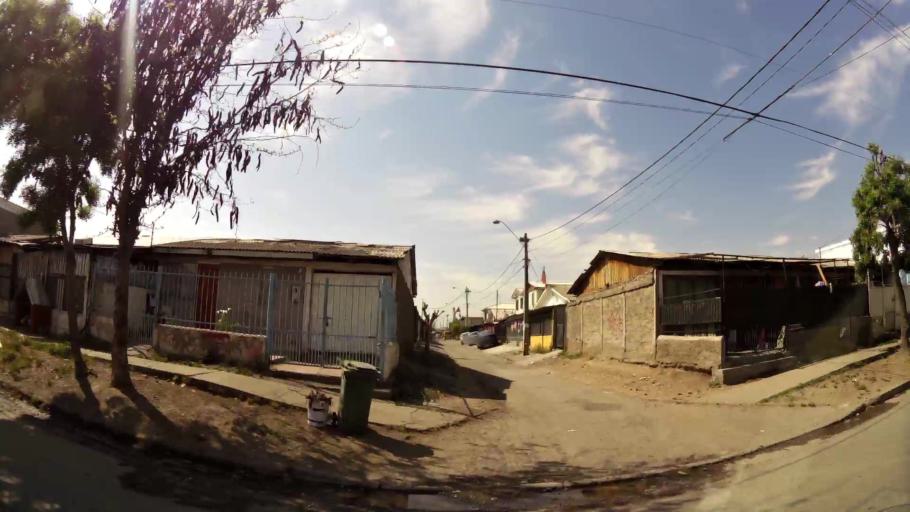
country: CL
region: Santiago Metropolitan
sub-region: Provincia de Santiago
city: La Pintana
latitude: -33.5629
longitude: -70.6448
